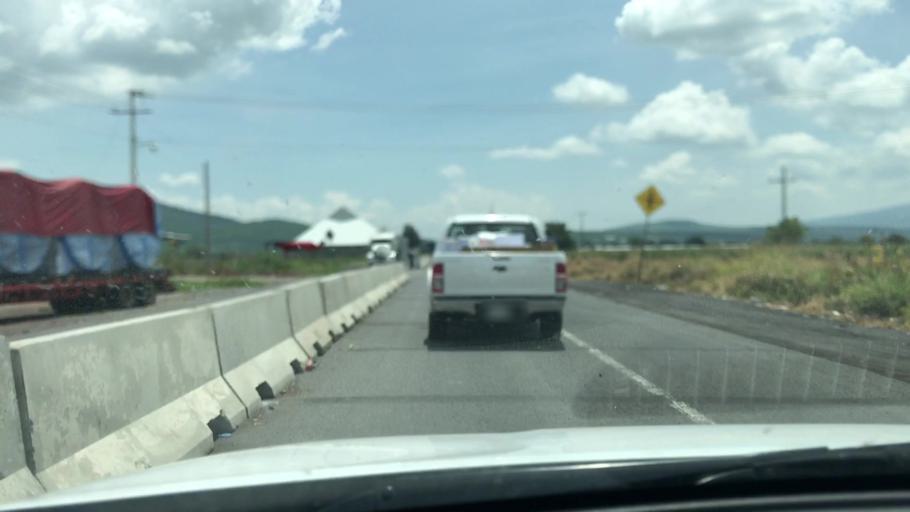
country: MX
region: Michoacan
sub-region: Yurecuaro
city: Yurecuaro
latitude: 20.3228
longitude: -102.2816
